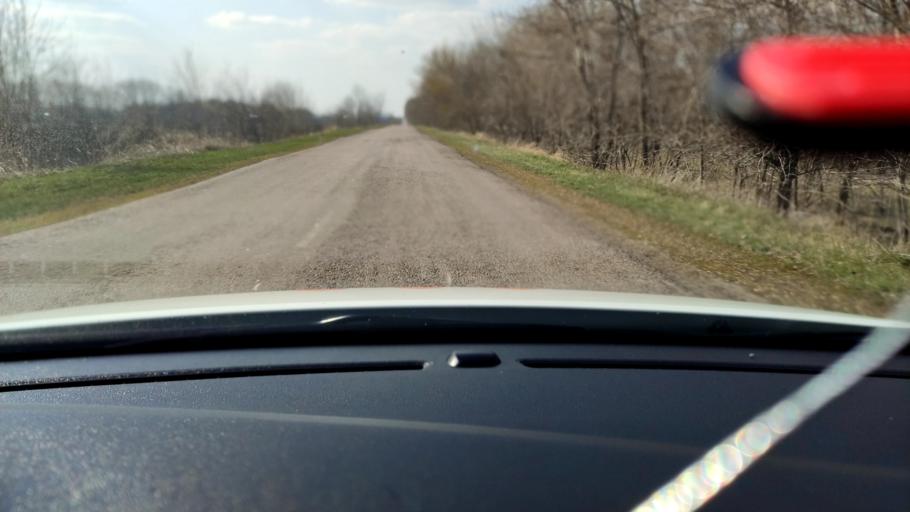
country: RU
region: Voronezj
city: Uryv-Pokrovka
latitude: 51.1219
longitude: 39.1277
